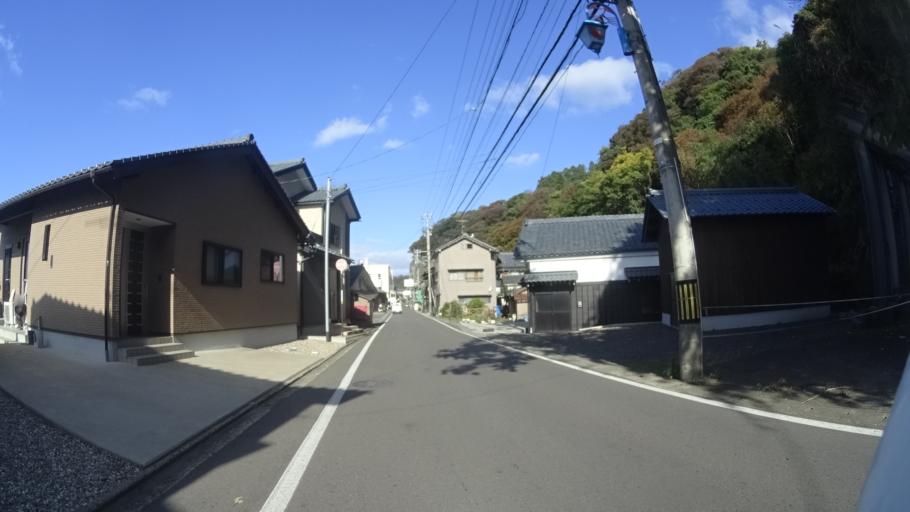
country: JP
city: Asahi
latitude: 35.9352
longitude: 135.9978
